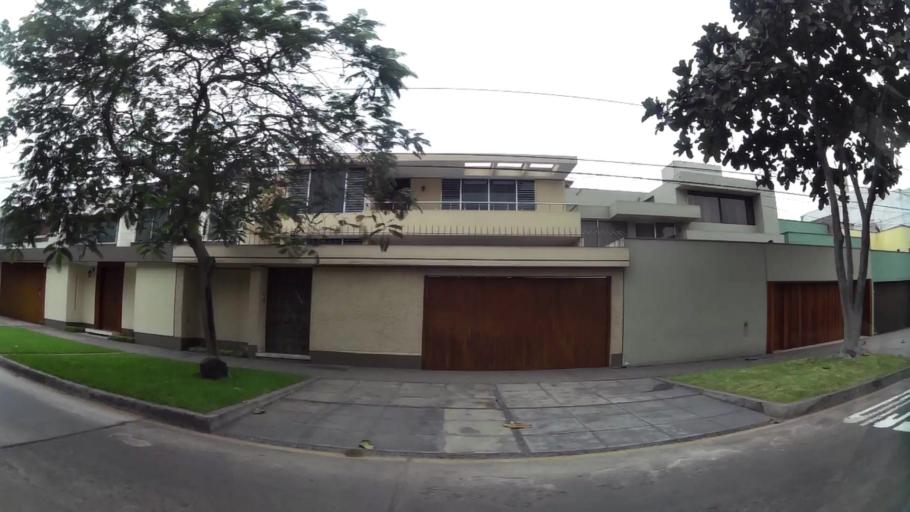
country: PE
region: Lima
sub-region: Lima
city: San Luis
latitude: -12.0894
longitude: -76.9919
